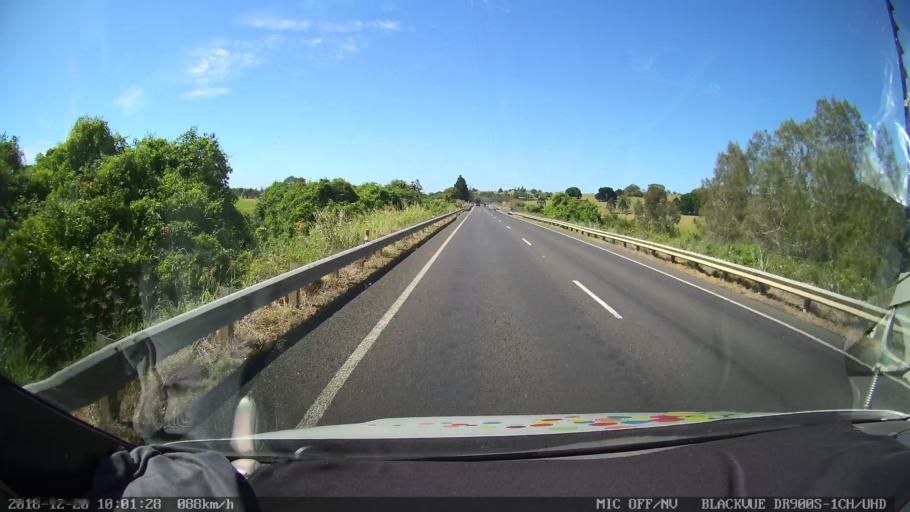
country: AU
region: New South Wales
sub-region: Lismore Municipality
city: Lismore
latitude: -28.8448
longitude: 153.2624
